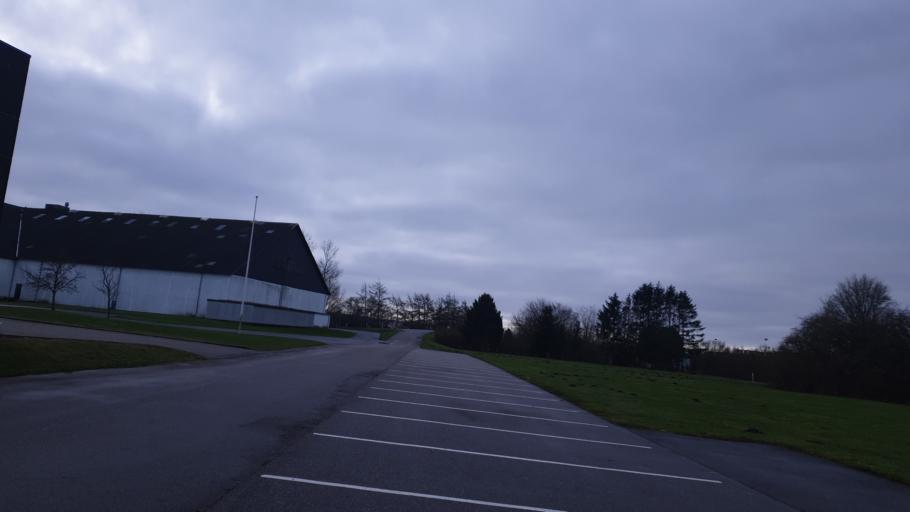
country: DK
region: Central Jutland
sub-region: Hedensted Kommune
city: Hedensted
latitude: 55.7806
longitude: 9.7004
